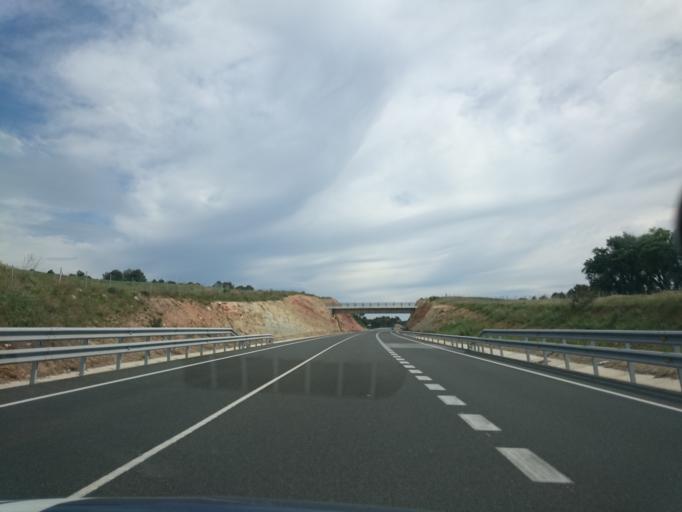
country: ES
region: Catalonia
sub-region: Provincia de Barcelona
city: Castelloli
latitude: 41.6241
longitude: 1.6851
